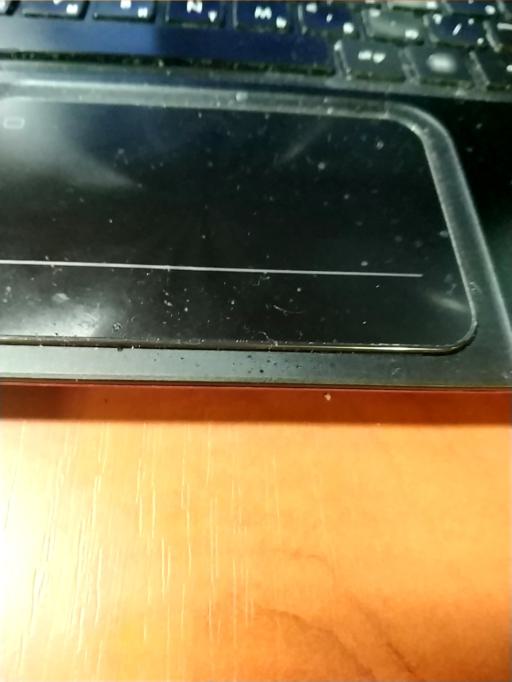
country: RU
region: Tverskaya
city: Likhoslavl'
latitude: 57.1624
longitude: 35.5756
